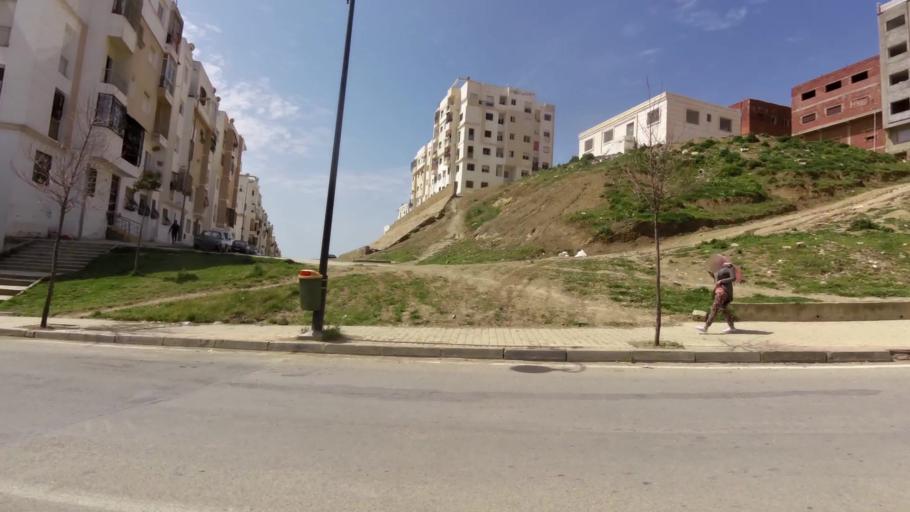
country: MA
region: Tanger-Tetouan
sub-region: Tanger-Assilah
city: Tangier
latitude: 35.7335
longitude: -5.8159
